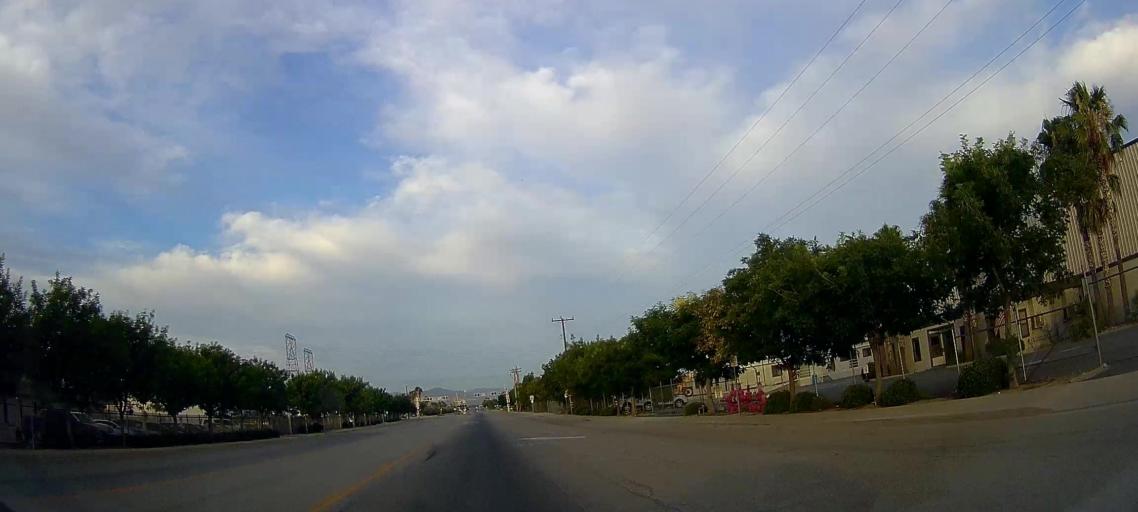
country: US
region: California
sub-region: Kern County
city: Bakersfield
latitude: 35.3543
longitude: -118.9255
